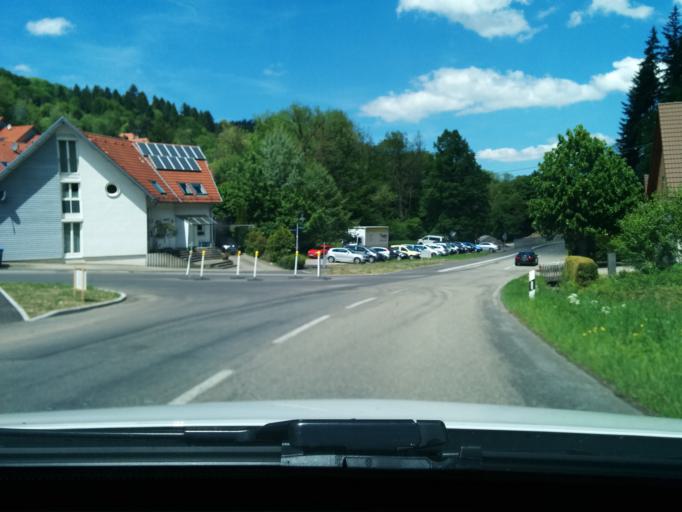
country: DE
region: Baden-Wuerttemberg
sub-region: Freiburg Region
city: Horben
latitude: 47.9401
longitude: 7.8682
